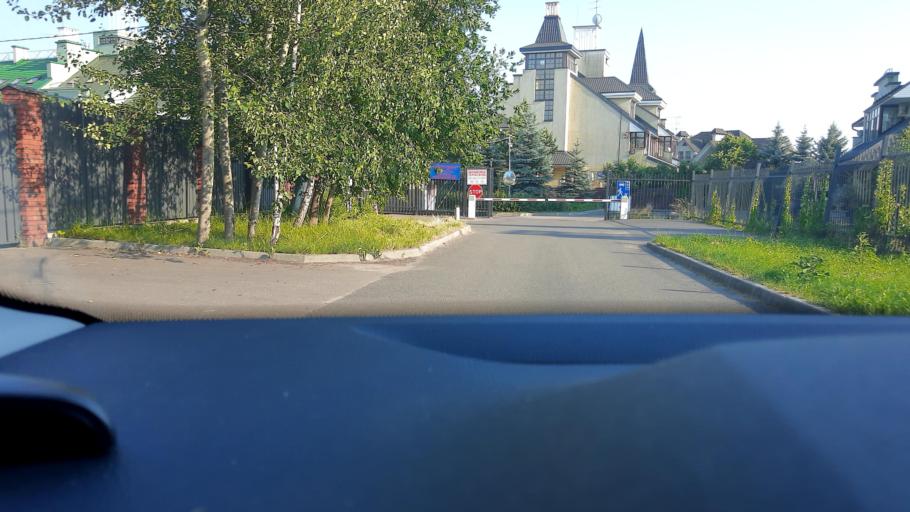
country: RU
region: Moskovskaya
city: Novopodrezkovo
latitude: 55.8975
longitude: 37.3754
